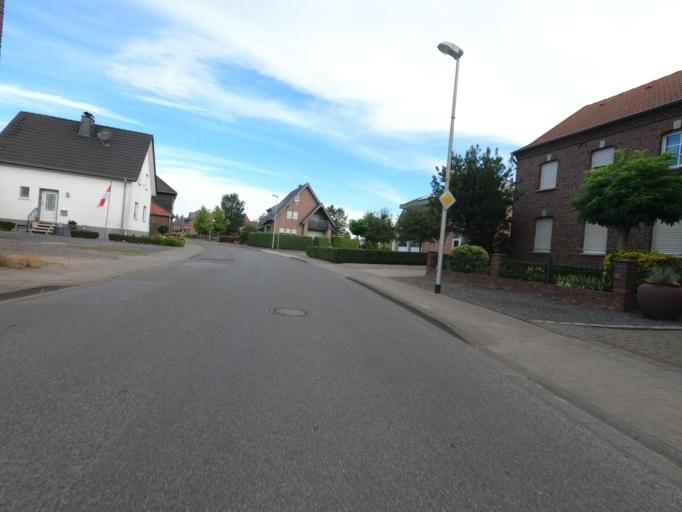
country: NL
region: Limburg
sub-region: Gemeente Roerdalen
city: Vlodrop
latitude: 51.1109
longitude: 6.1013
